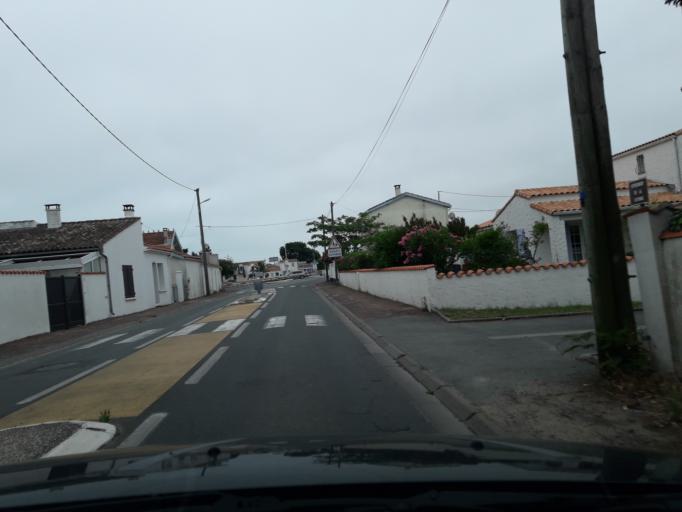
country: FR
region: Poitou-Charentes
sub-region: Departement de la Charente-Maritime
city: Boyard-Ville
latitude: 45.9652
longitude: -1.2454
